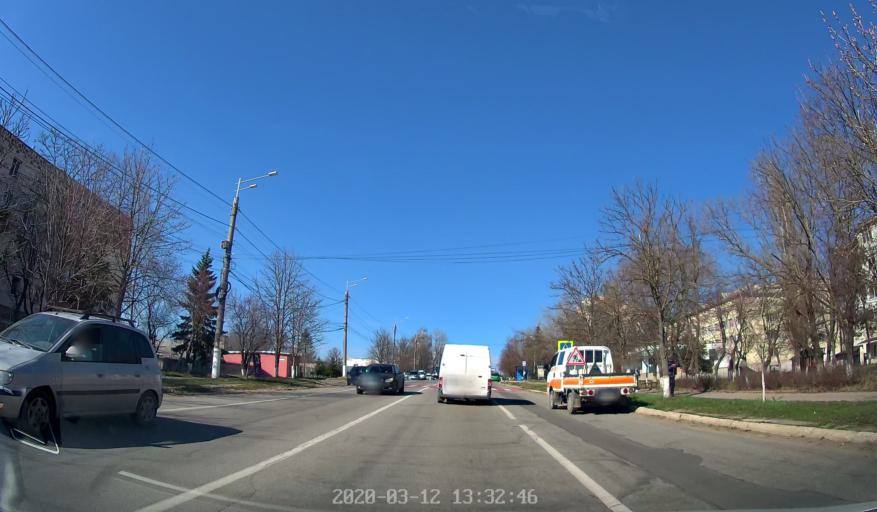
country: MD
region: Laloveni
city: Ialoveni
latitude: 46.9529
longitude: 28.7708
